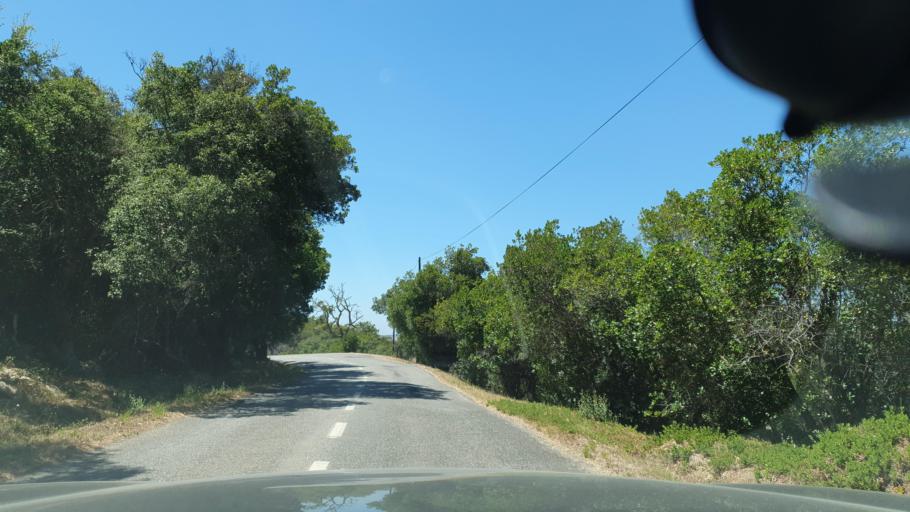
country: PT
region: Beja
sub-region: Odemira
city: Odemira
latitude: 37.5978
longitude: -8.5711
